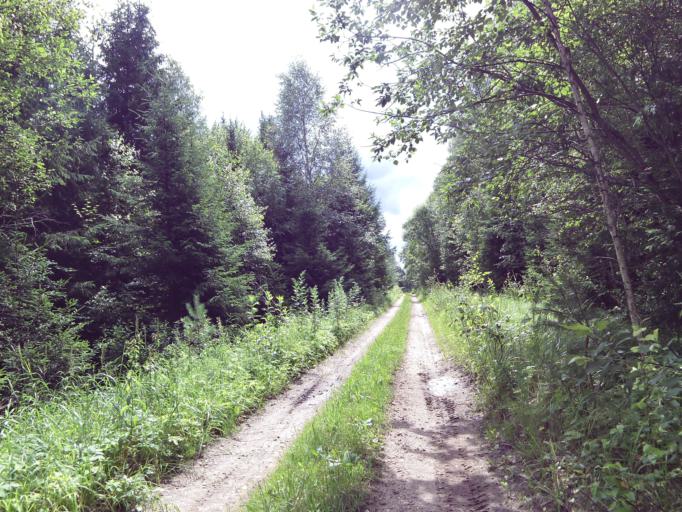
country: RU
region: Moskovskaya
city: Popovo
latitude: 54.9727
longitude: 37.6962
